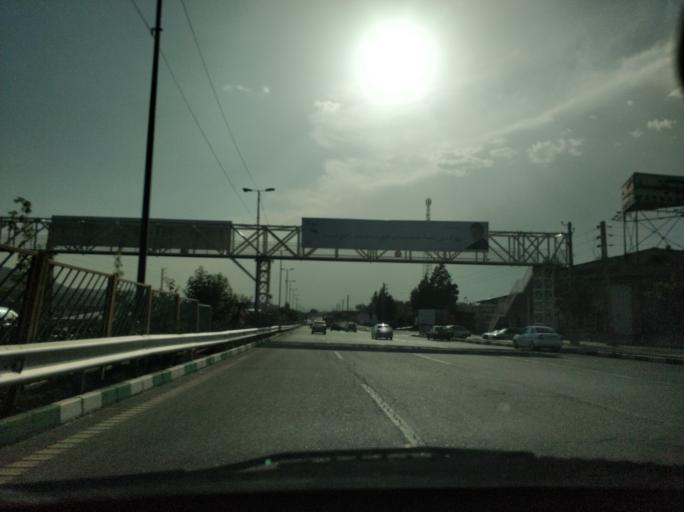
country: IR
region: Tehran
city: Tehran
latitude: 35.7238
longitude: 51.5815
